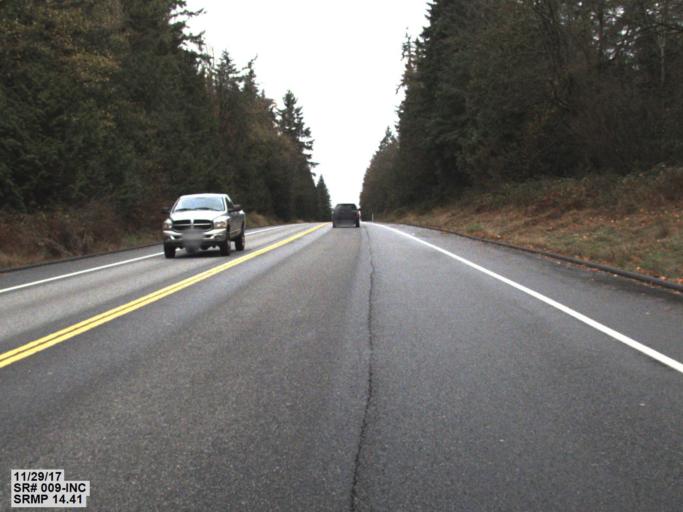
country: US
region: Washington
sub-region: Snohomish County
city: West Lake Stevens
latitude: 47.9835
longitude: -122.1031
